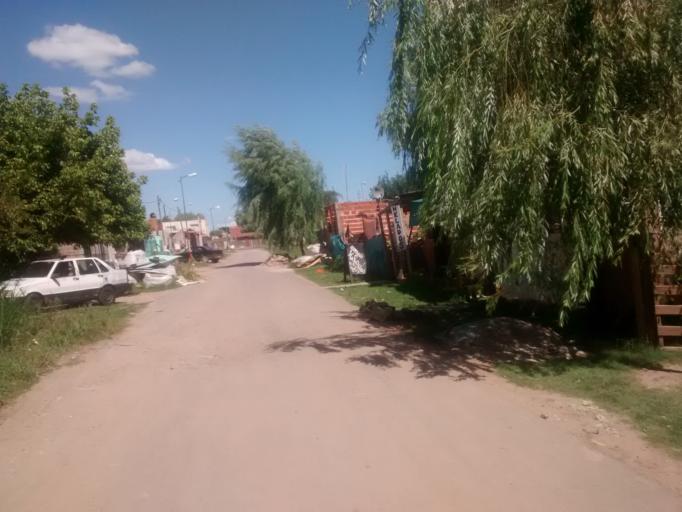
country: AR
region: Buenos Aires
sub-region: Partido de La Plata
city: La Plata
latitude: -34.9447
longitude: -57.9279
